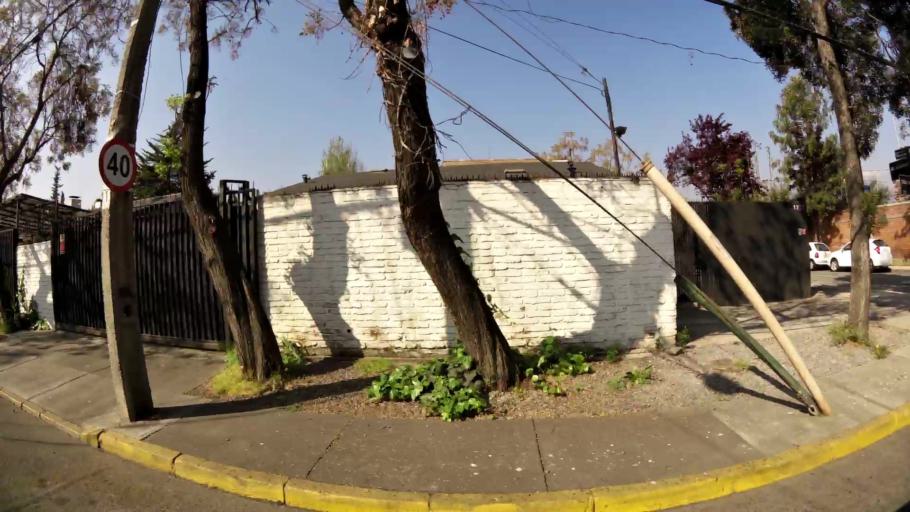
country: CL
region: Santiago Metropolitan
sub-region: Provincia de Santiago
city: Villa Presidente Frei, Nunoa, Santiago, Chile
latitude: -33.3966
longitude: -70.5731
